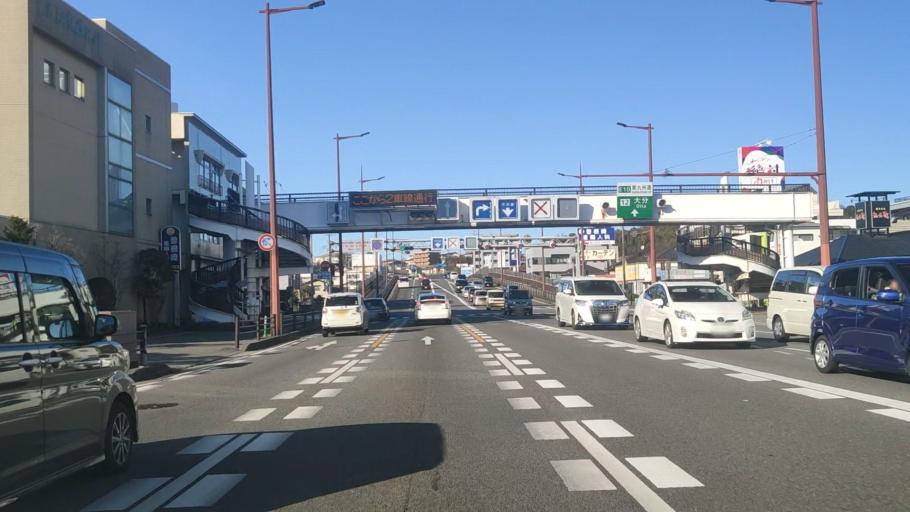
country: JP
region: Oita
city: Oita
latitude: 33.2152
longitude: 131.5958
